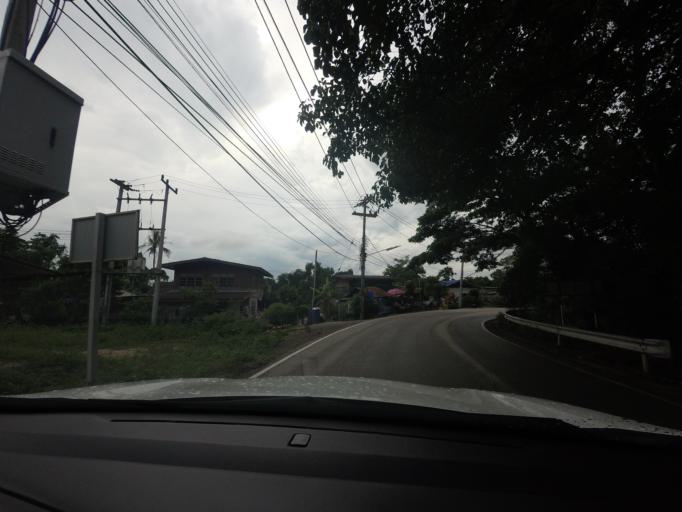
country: TH
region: Nakhon Ratchasima
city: Pak Chong
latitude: 14.6127
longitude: 101.4451
